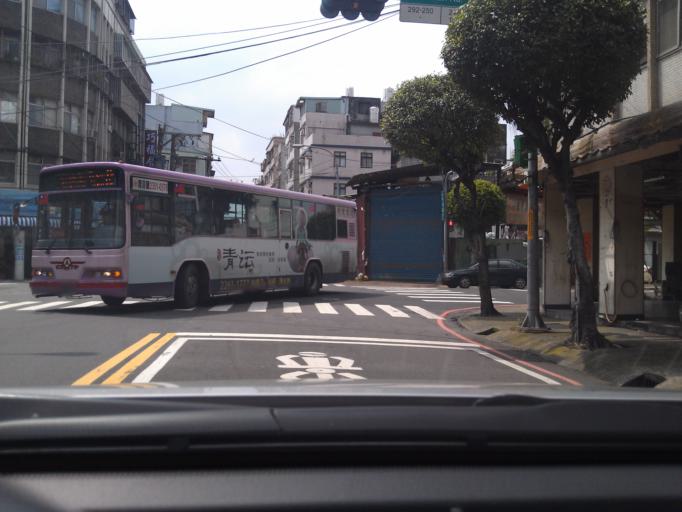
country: TW
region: Taipei
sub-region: Taipei
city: Banqiao
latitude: 25.0127
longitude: 121.5068
